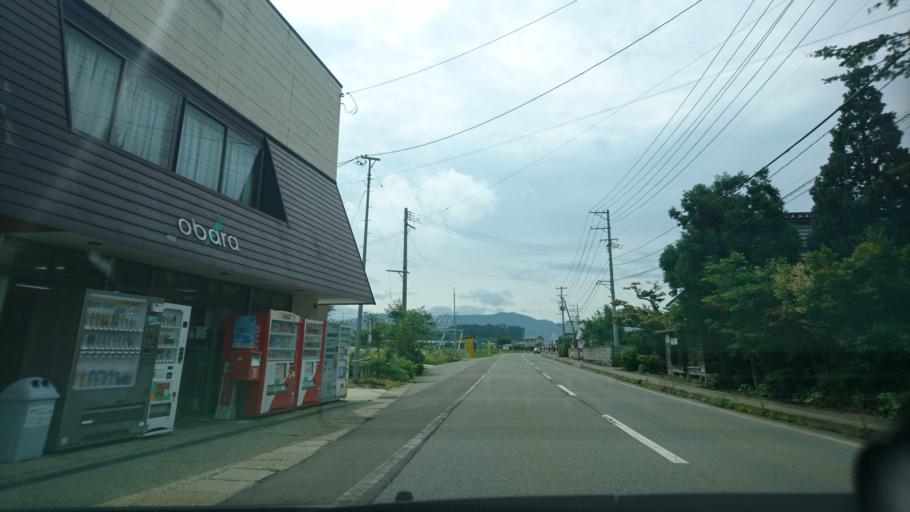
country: JP
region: Akita
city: Yuzawa
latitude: 39.1913
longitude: 140.5500
